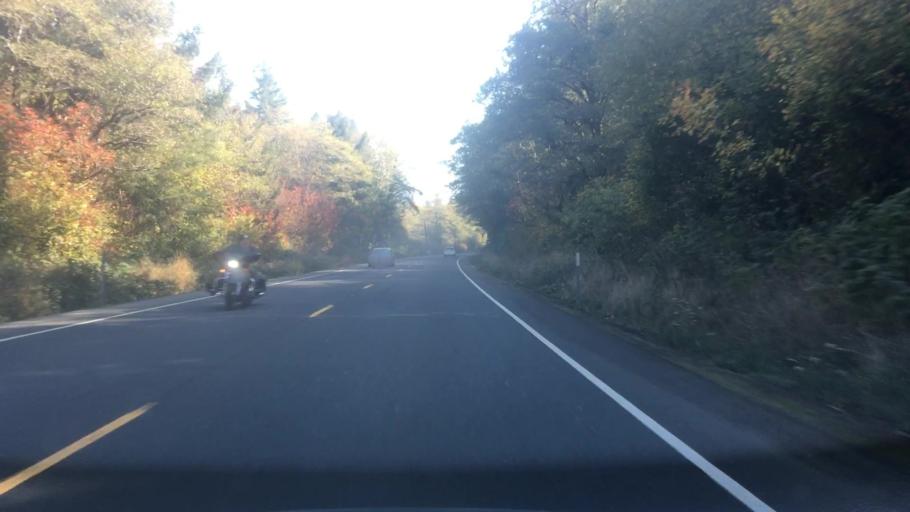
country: US
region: Oregon
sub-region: Lincoln County
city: Rose Lodge
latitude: 45.0117
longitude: -123.9259
